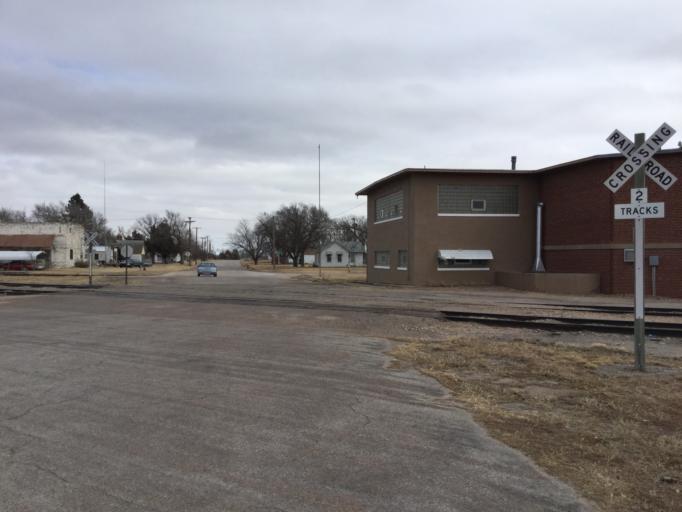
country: US
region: Kansas
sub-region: Pawnee County
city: Larned
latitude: 38.1796
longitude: -99.0952
